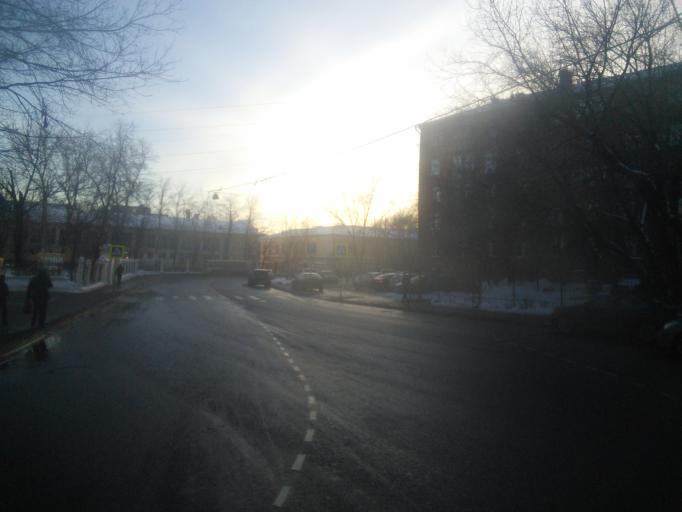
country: RU
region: Moscow
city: Lefortovo
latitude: 55.7644
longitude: 37.6711
